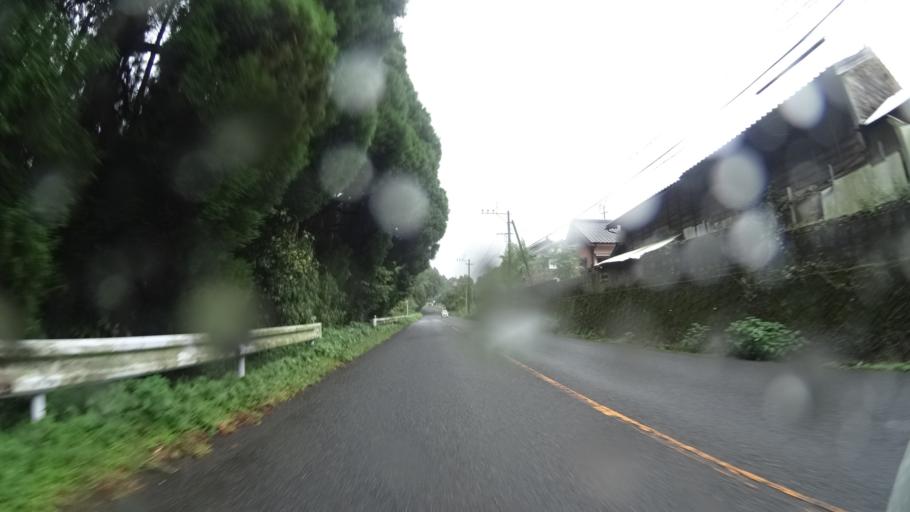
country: JP
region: Kagoshima
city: Kajiki
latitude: 31.7884
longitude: 130.6760
